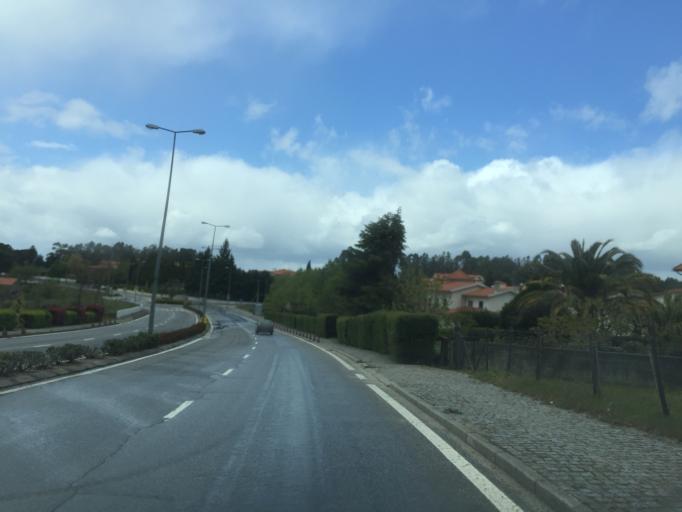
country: PT
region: Guarda
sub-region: Manteigas
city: Manteigas
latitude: 40.5007
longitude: -7.6050
